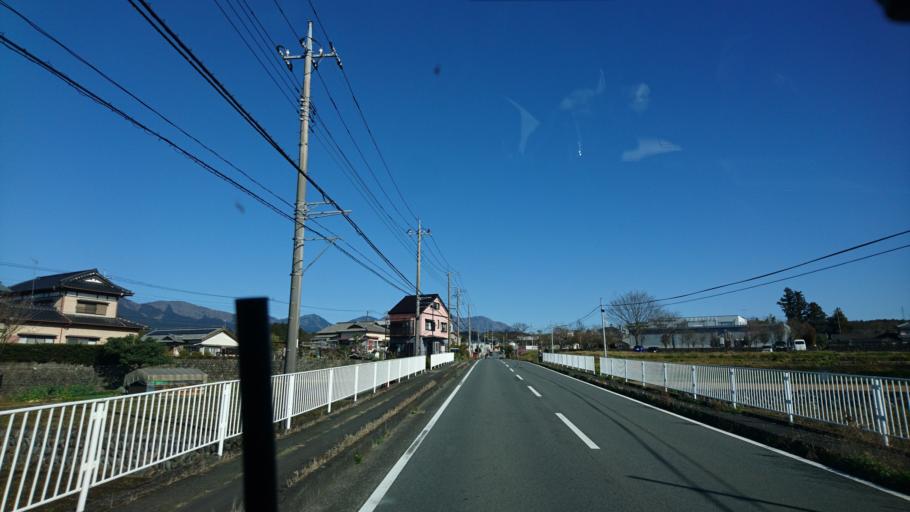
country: JP
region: Shizuoka
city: Fujinomiya
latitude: 35.2823
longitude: 138.6035
